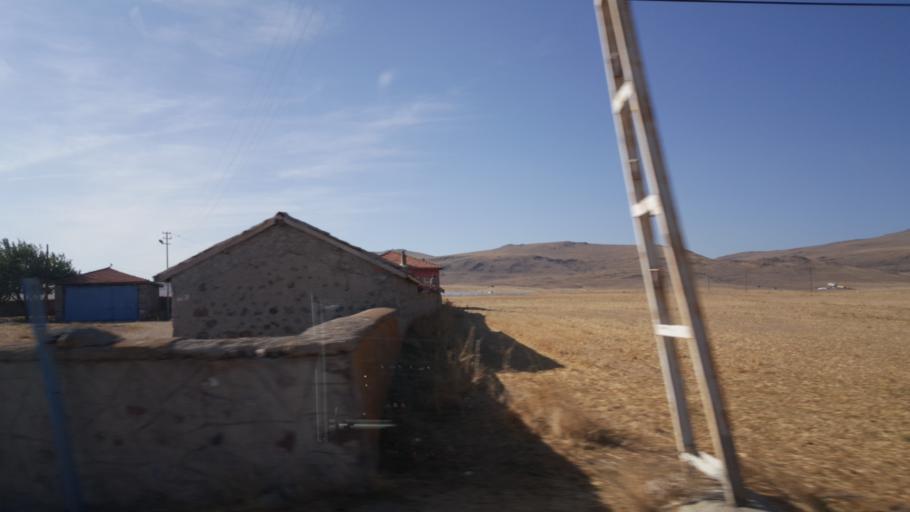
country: TR
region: Ankara
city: Altpinar
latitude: 39.2664
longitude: 32.7537
